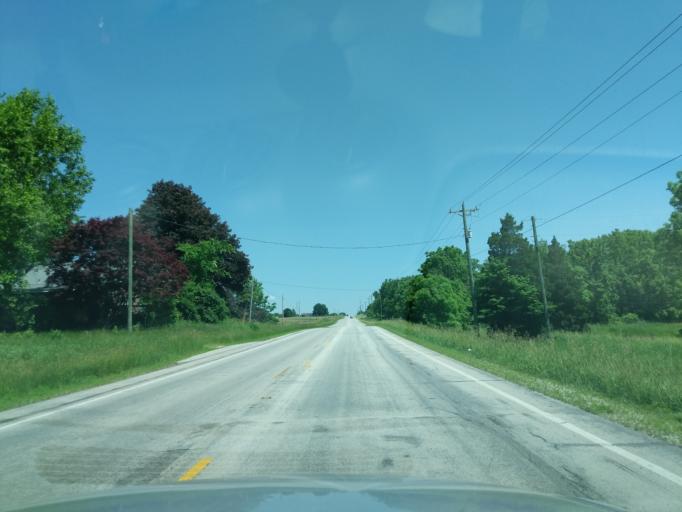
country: US
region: Indiana
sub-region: Whitley County
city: Columbia City
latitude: 41.2014
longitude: -85.4917
